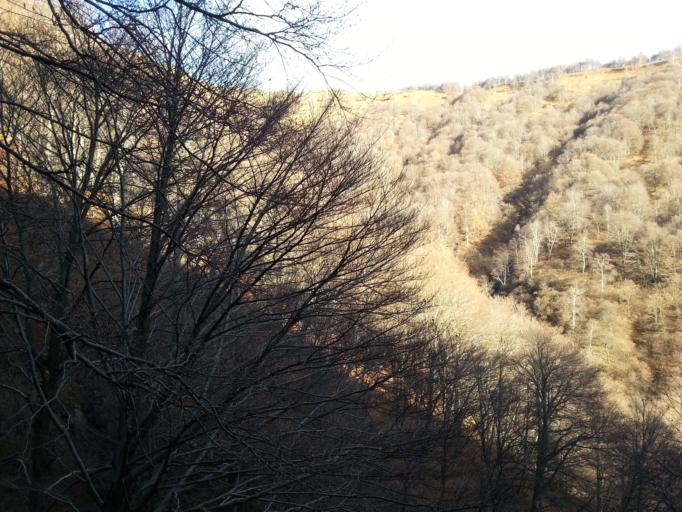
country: CH
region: Ticino
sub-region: Lugano District
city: Gravesano
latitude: 46.0540
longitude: 8.8693
